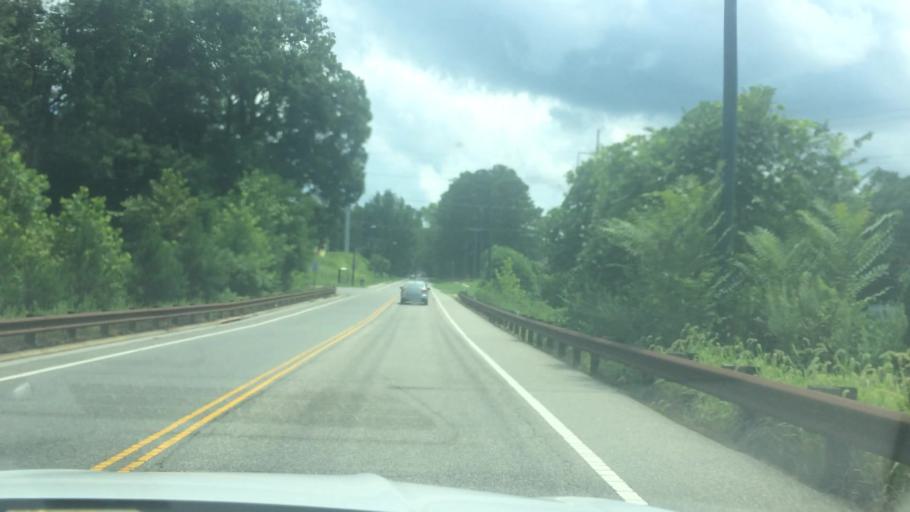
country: US
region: Virginia
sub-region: City of Williamsburg
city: Williamsburg
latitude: 37.2843
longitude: -76.6849
